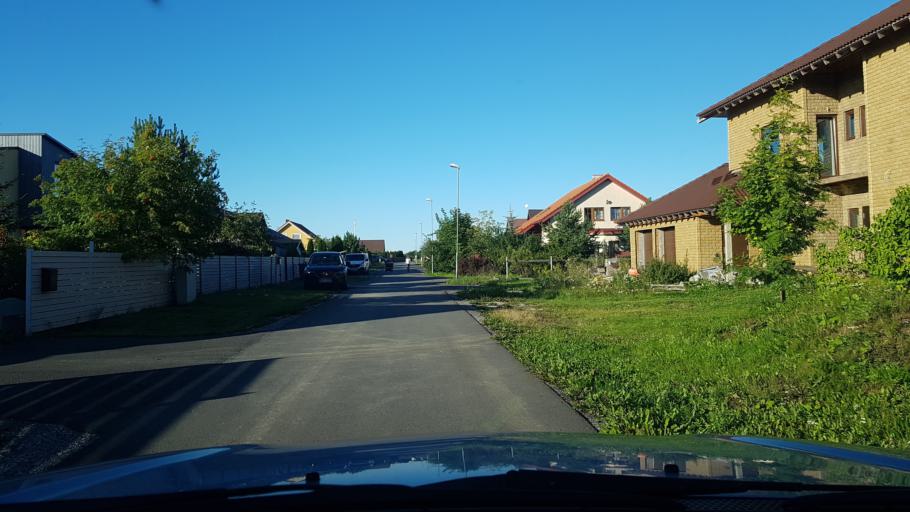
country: EE
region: Harju
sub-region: Rae vald
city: Jueri
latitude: 59.3837
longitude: 24.8451
